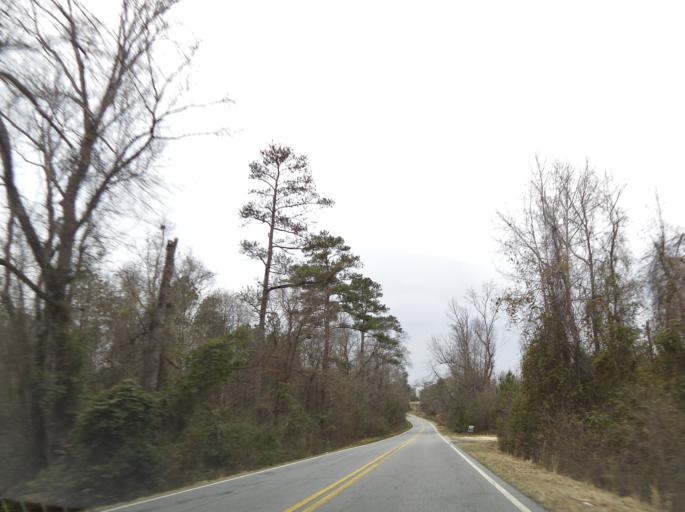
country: US
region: Georgia
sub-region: Peach County
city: Byron
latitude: 32.7170
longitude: -83.7048
